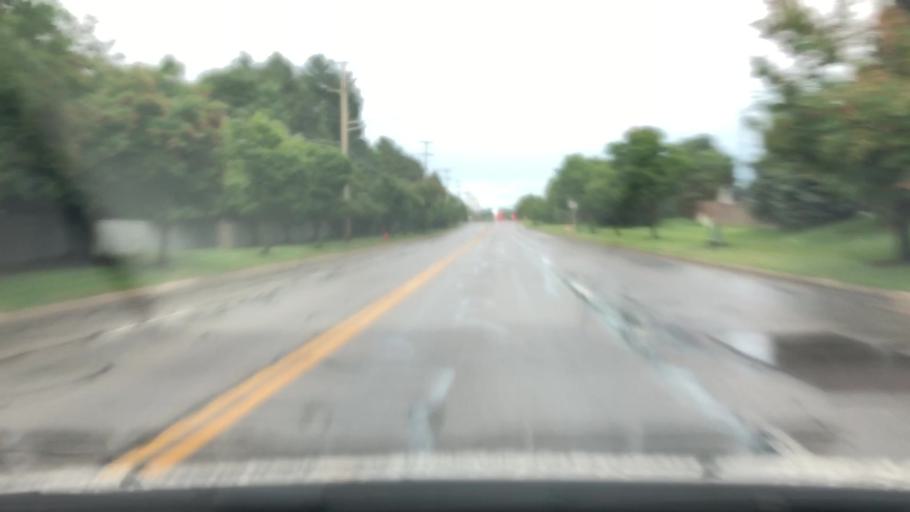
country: US
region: Ohio
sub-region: Franklin County
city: Westerville
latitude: 40.1316
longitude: -82.8912
